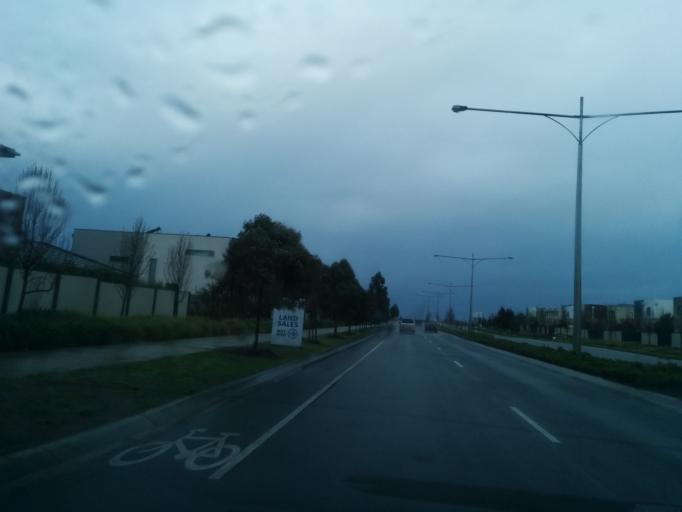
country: AU
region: Victoria
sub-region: Wyndham
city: Point Cook
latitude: -37.9105
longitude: 144.7572
